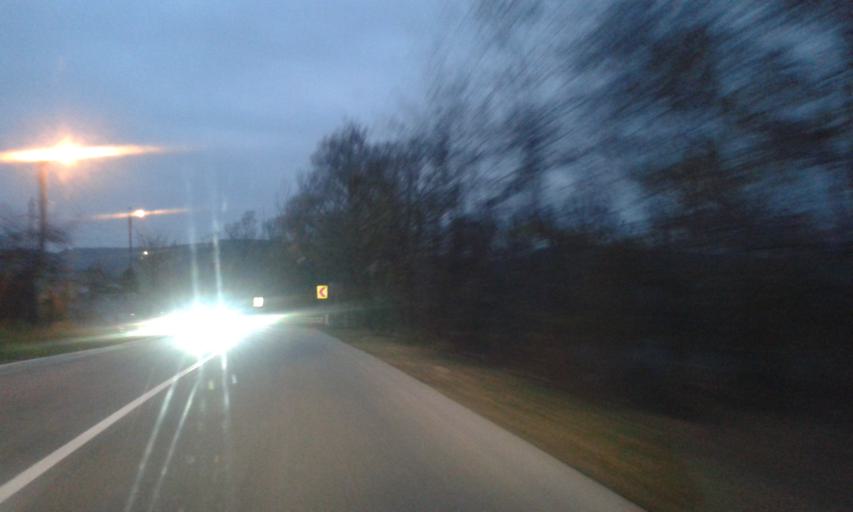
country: RO
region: Gorj
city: Targu Jiu
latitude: 45.0760
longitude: 23.2983
